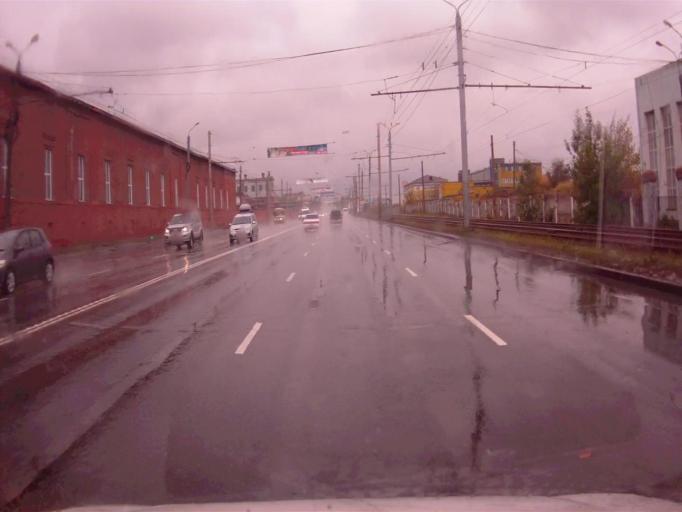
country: RU
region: Chelyabinsk
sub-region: Gorod Chelyabinsk
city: Chelyabinsk
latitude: 55.2083
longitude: 61.3840
